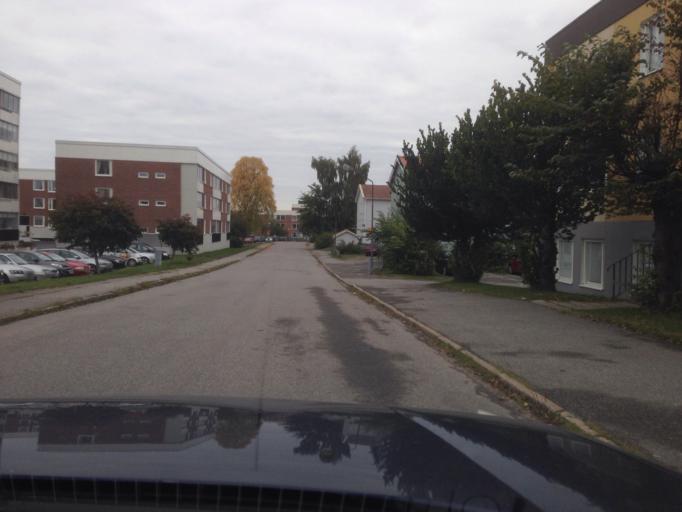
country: SE
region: Vaesternorrland
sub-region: Sundsvalls Kommun
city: Sundsvall
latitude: 62.4006
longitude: 17.3299
